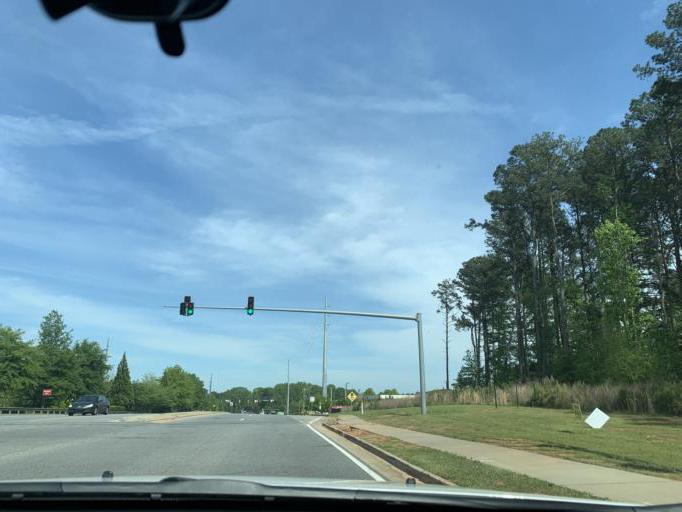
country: US
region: Georgia
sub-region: Forsyth County
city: Cumming
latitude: 34.1511
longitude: -84.1764
